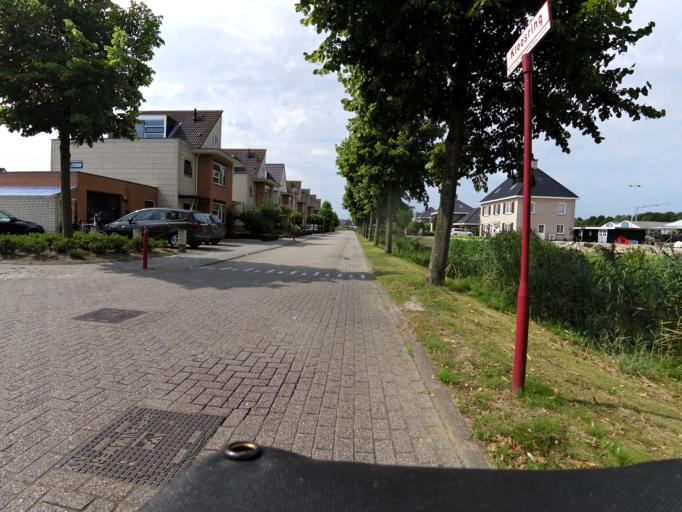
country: NL
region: South Holland
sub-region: Gemeente Oud-Beijerland
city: Oud-Beijerland
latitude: 51.8203
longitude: 4.4330
